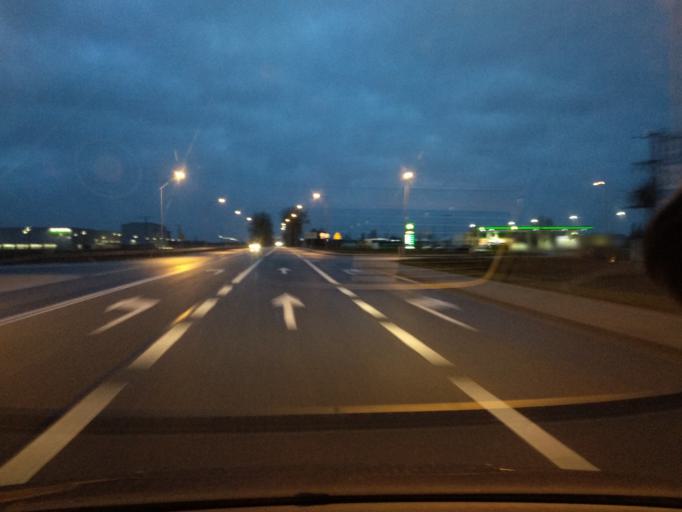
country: PL
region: Lower Silesian Voivodeship
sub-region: Powiat sredzki
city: Mrozow
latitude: 51.1535
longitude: 16.8155
